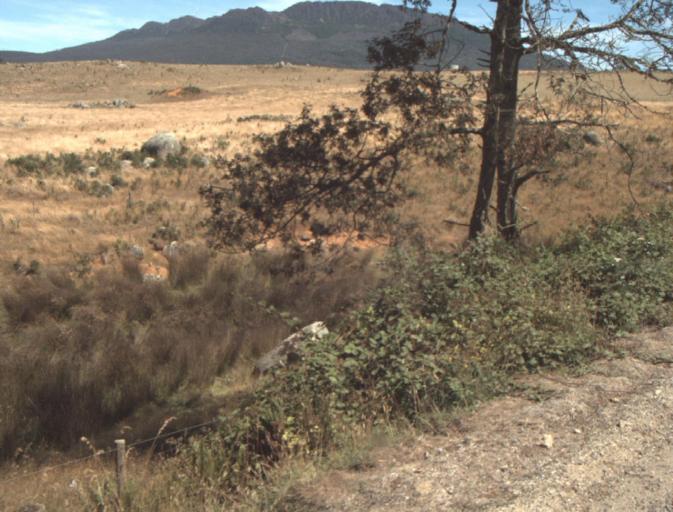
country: AU
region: Tasmania
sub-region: Dorset
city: Scottsdale
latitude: -41.3226
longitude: 147.4499
